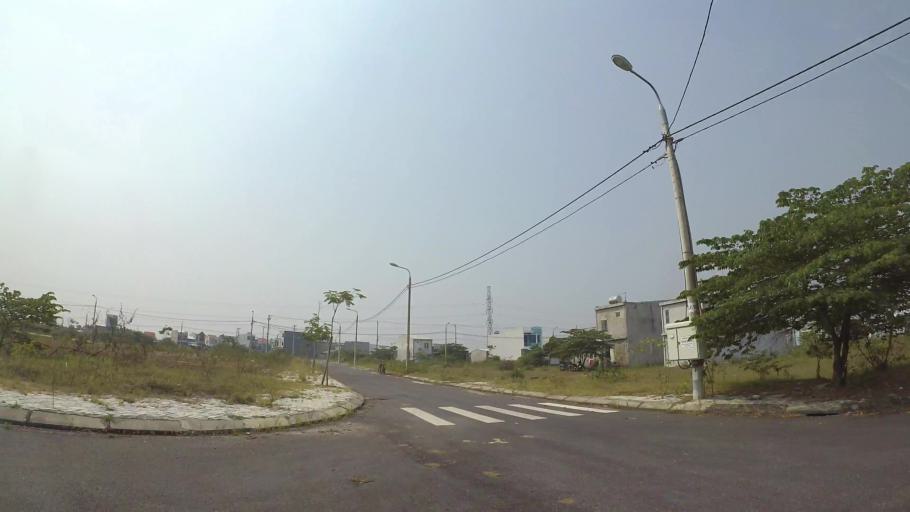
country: VN
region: Da Nang
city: Cam Le
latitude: 15.9708
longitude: 108.2138
